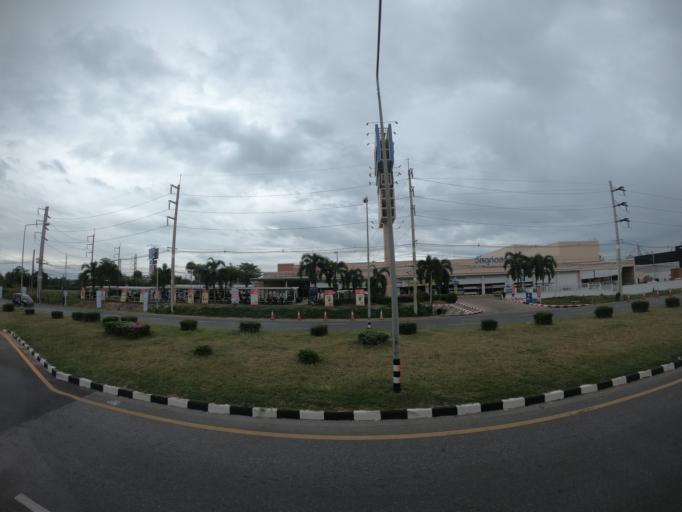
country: TH
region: Roi Et
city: Roi Et
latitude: 16.0619
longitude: 103.6191
